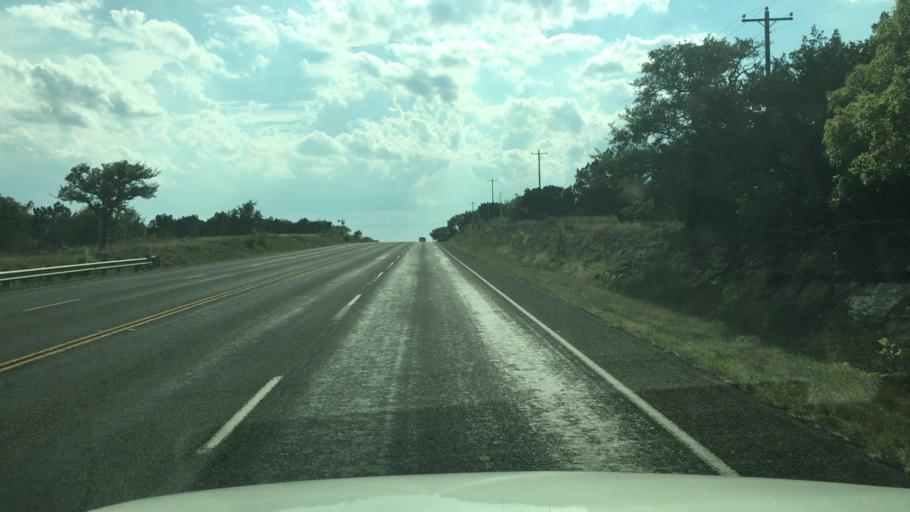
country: US
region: Texas
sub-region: Blanco County
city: Johnson City
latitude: 30.2091
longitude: -98.2963
